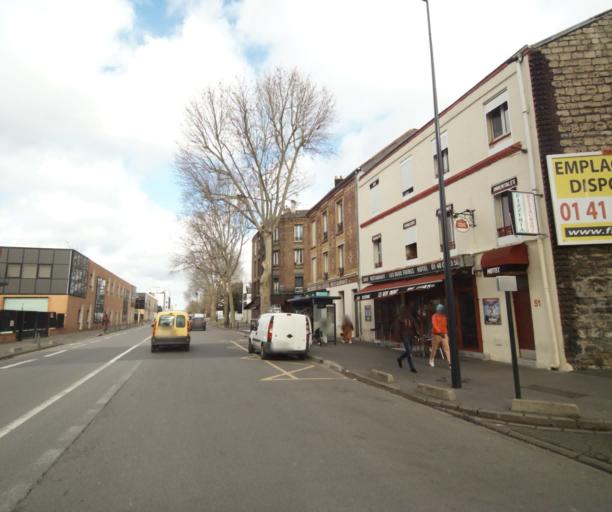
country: FR
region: Ile-de-France
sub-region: Departement de Seine-Saint-Denis
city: Saint-Denis
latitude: 48.9263
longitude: 2.3419
